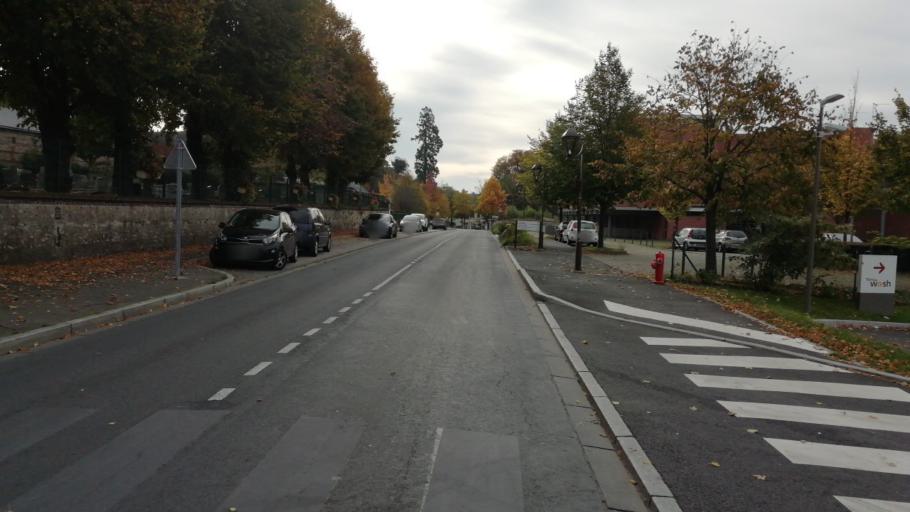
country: FR
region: Haute-Normandie
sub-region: Departement de la Seine-Maritime
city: Harfleur
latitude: 49.5109
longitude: 0.2001
